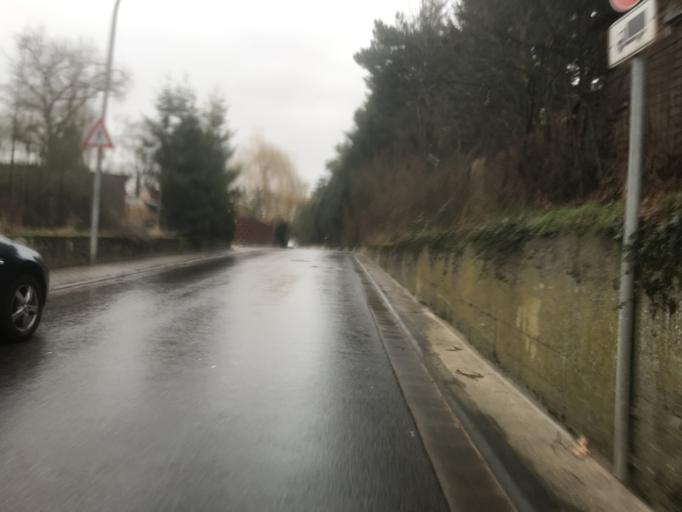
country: DE
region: Rheinland-Pfalz
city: Budenheim
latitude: 50.0074
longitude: 8.1391
